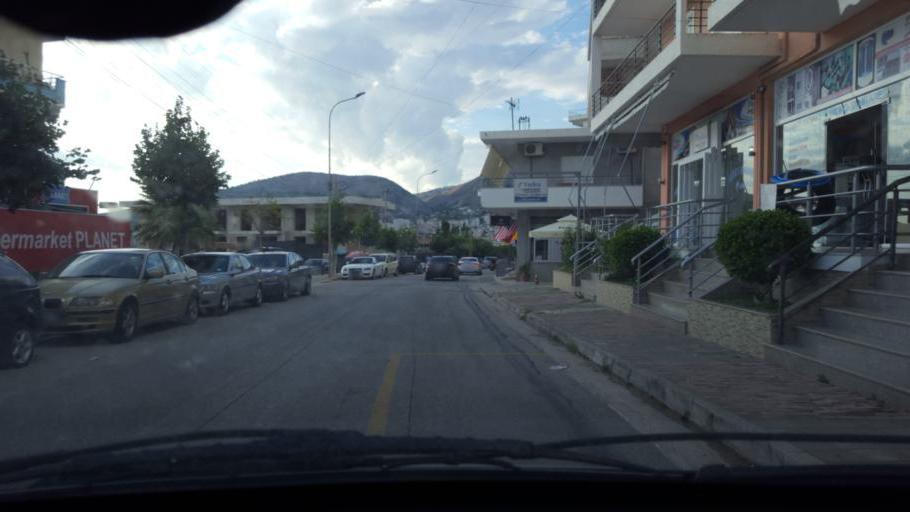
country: AL
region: Vlore
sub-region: Rrethi i Sarandes
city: Sarande
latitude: 39.8645
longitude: 20.0170
